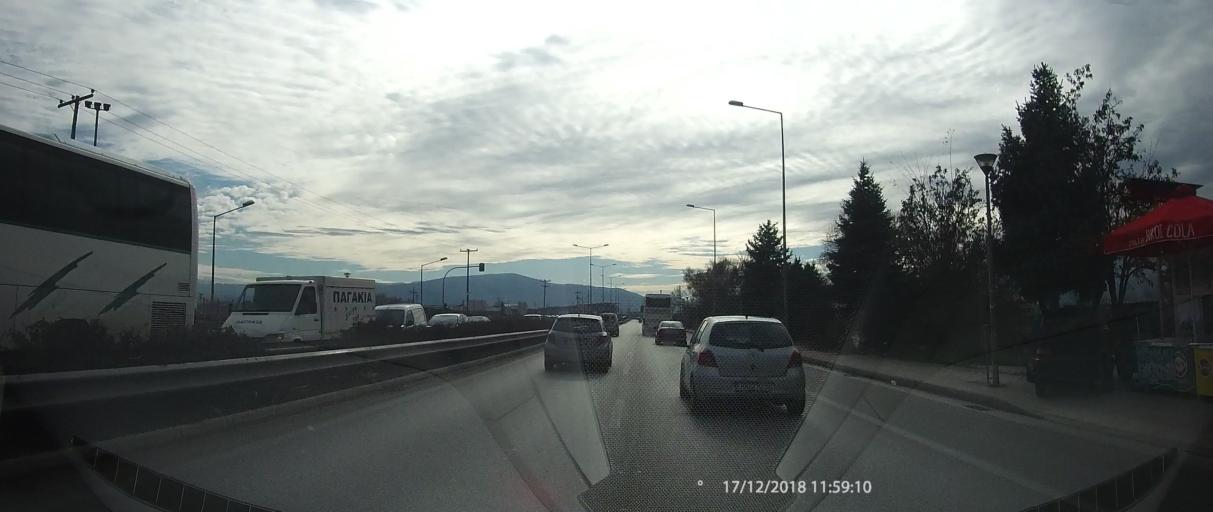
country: GR
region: Epirus
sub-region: Nomos Ioanninon
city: Anatoli
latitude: 39.6218
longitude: 20.8611
